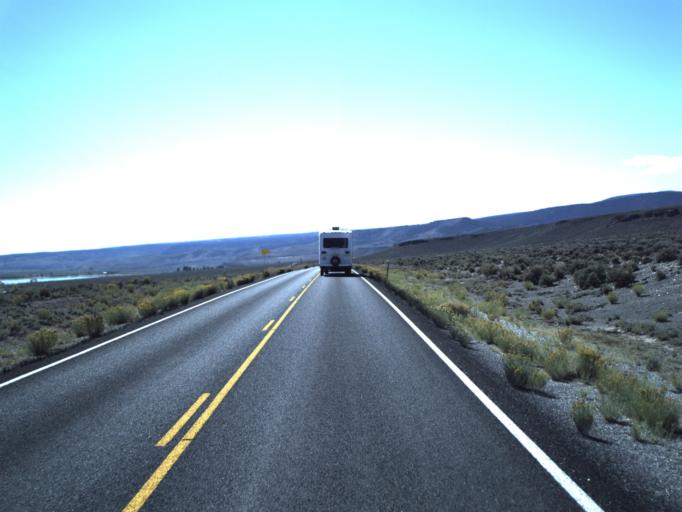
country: US
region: Utah
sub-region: Piute County
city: Junction
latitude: 38.1963
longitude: -112.0099
